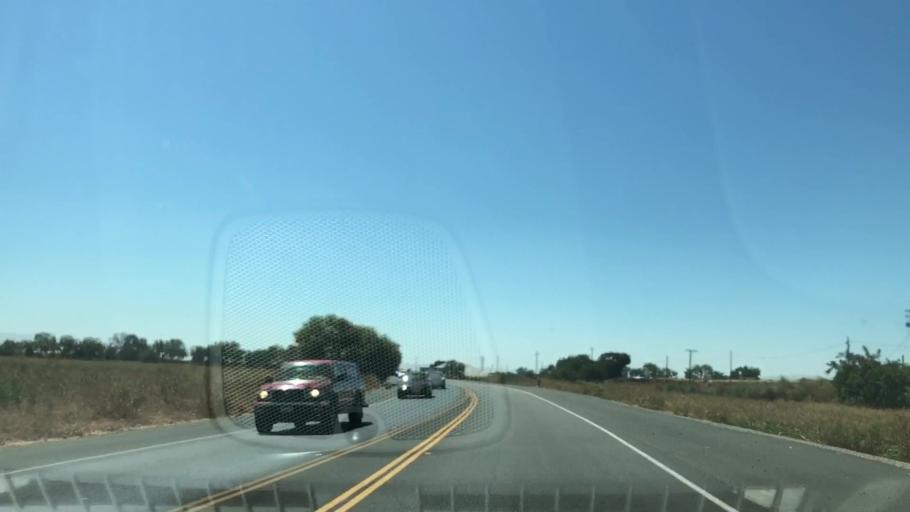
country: US
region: California
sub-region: San Joaquin County
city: Country Club
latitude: 37.9257
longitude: -121.4309
